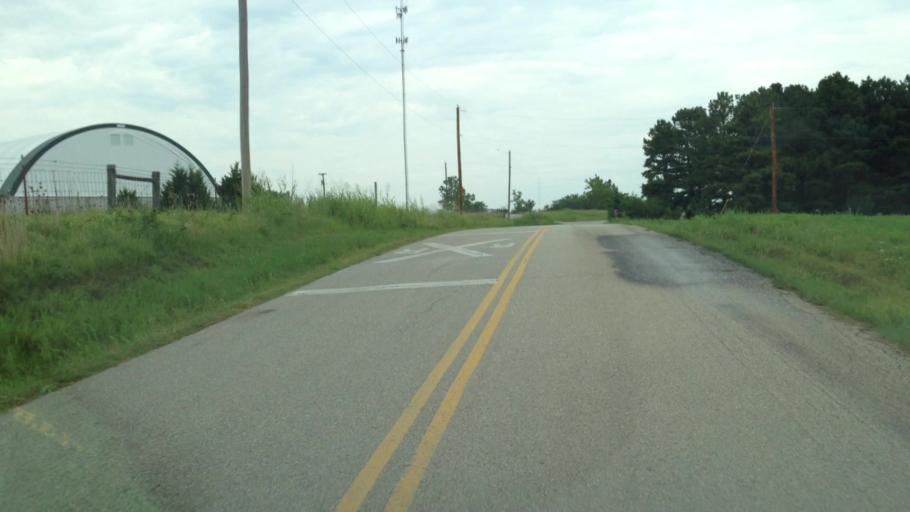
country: US
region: Oklahoma
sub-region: Craig County
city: Vinita
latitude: 36.6349
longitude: -95.1256
